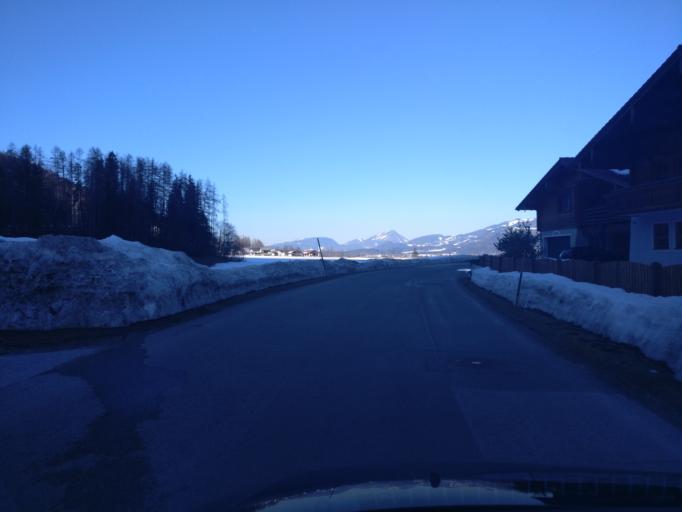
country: AT
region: Salzburg
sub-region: Politischer Bezirk Hallein
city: Kuchl
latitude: 47.6044
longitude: 13.1425
